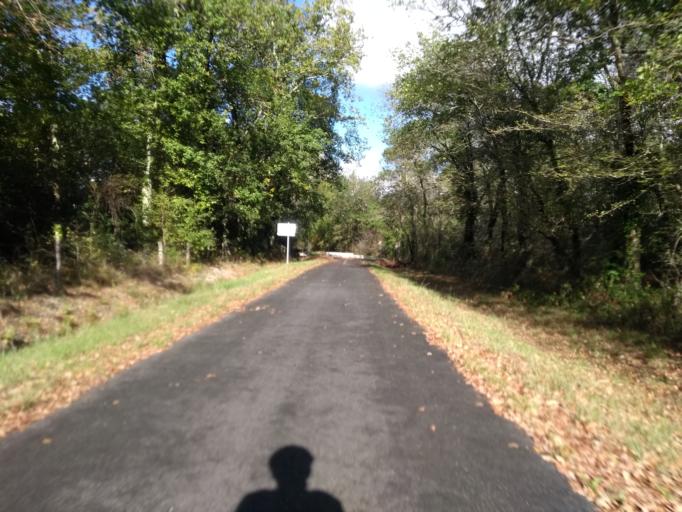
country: FR
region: Aquitaine
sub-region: Departement de la Gironde
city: Saint-Aubin-de-Medoc
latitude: 44.8081
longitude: -0.7062
